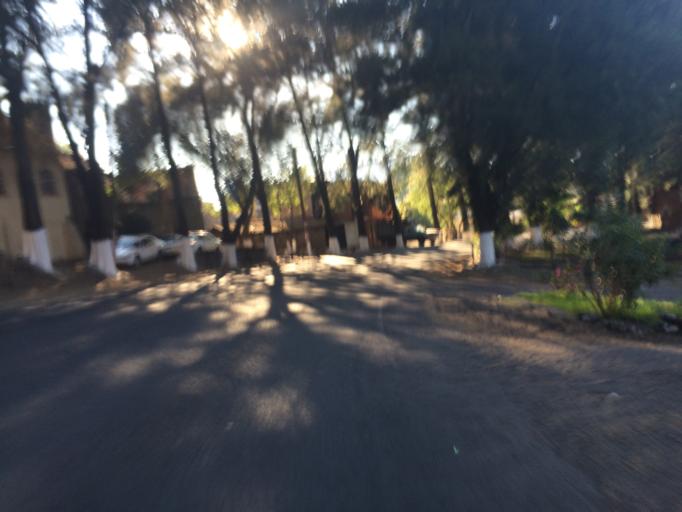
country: MX
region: Michoacan
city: Patzcuaro
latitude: 19.5057
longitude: -101.6128
